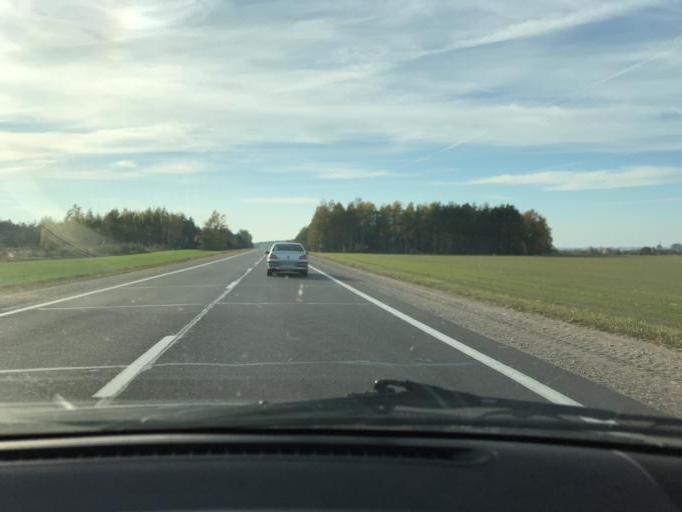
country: BY
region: Brest
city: Horad Pinsk
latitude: 52.1658
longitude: 25.9961
